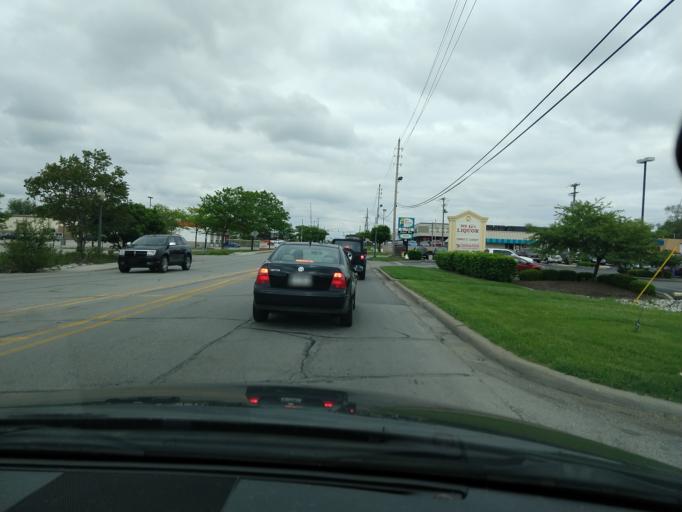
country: US
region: Indiana
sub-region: Hamilton County
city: Noblesville
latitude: 40.0455
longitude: -85.9985
